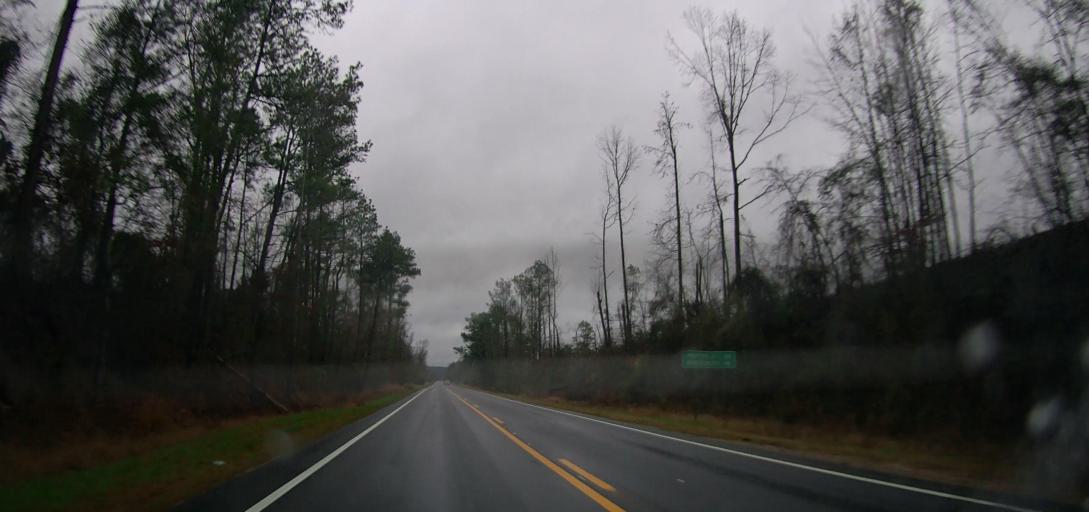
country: US
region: Alabama
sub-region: Chilton County
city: Thorsby
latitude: 32.7660
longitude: -86.8779
